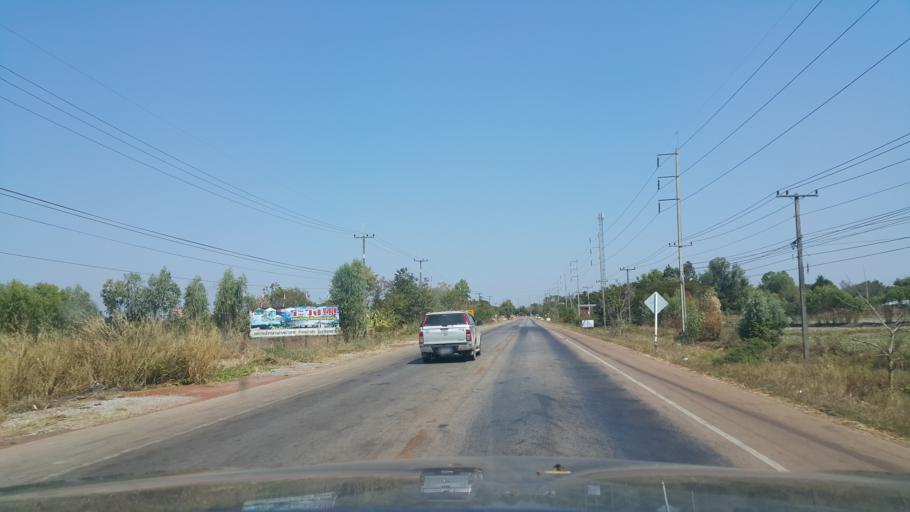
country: TH
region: Changwat Udon Thani
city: Thung Fon
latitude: 17.5374
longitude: 103.2315
